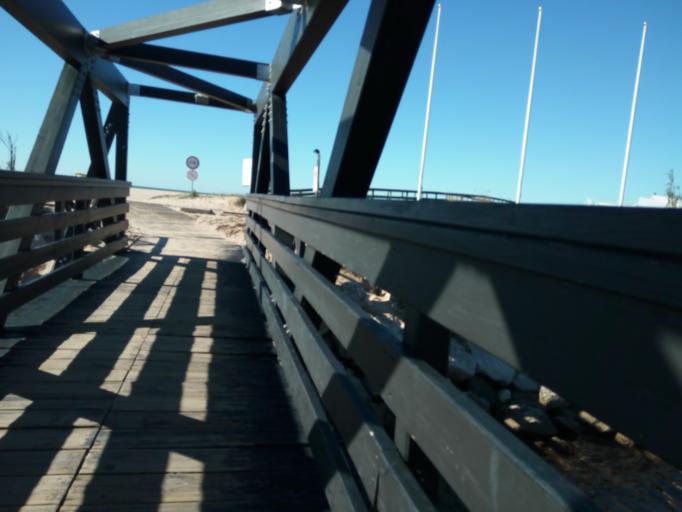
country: PT
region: Faro
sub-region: Loule
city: Vilamoura
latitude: 37.0744
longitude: -8.1256
